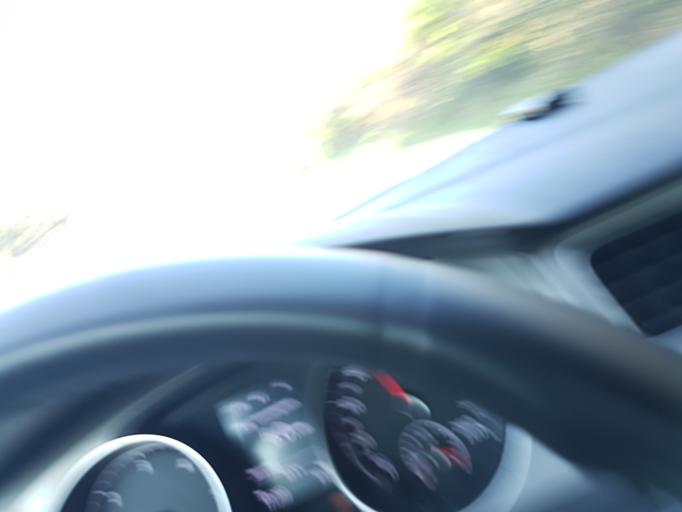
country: HU
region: Fejer
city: Fehervarcsurgo
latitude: 47.3299
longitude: 18.3152
